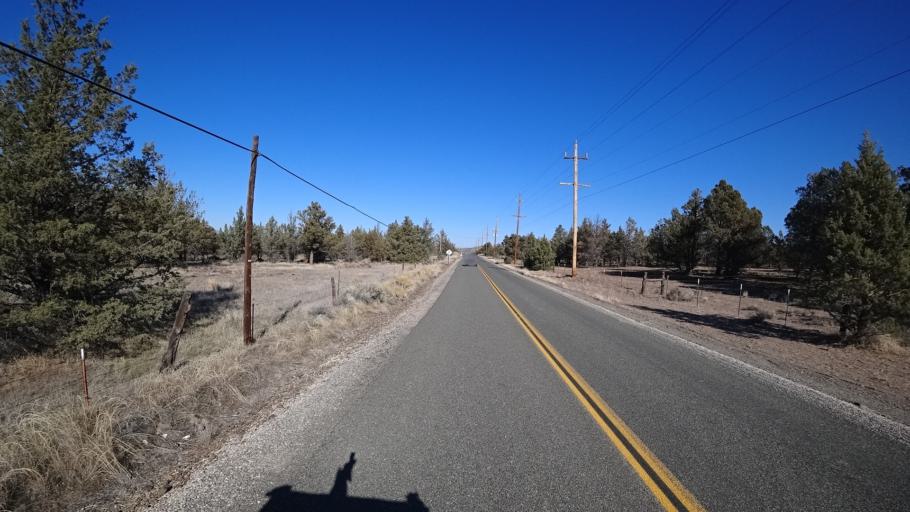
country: US
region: California
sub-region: Siskiyou County
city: Montague
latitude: 41.6634
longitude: -122.3691
